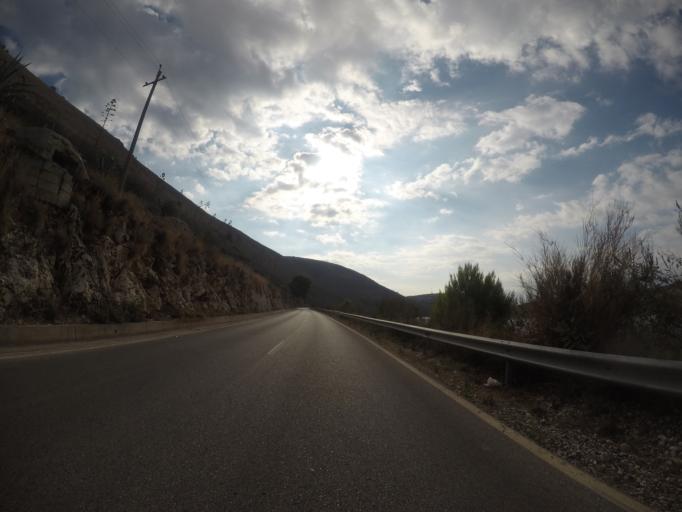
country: AL
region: Vlore
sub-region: Rrethi i Vlores
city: Himare
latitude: 40.0608
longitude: 19.7973
